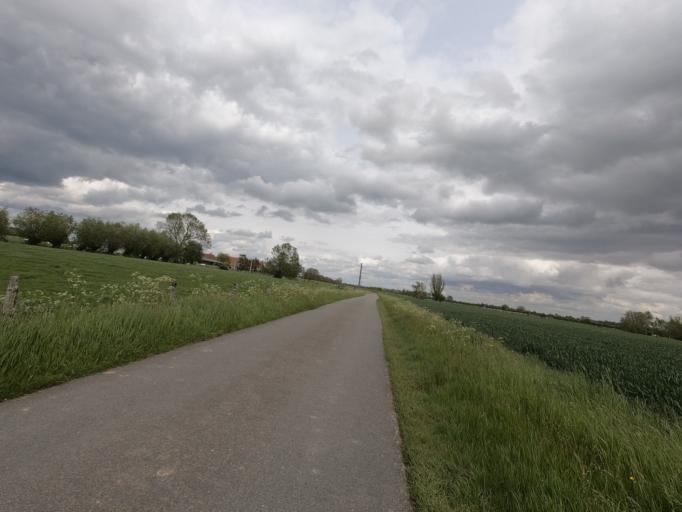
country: BE
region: Flanders
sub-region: Provincie West-Vlaanderen
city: Alveringem
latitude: 50.9434
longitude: 2.7314
